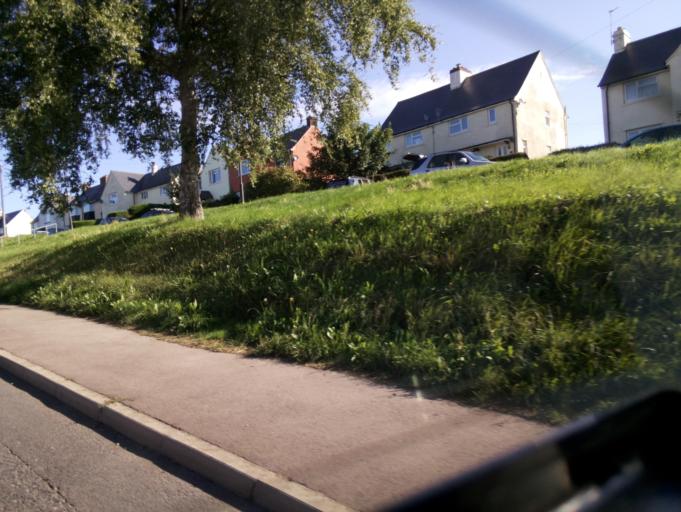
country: GB
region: England
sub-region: Gloucestershire
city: Coleford
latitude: 51.7969
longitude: -2.6206
